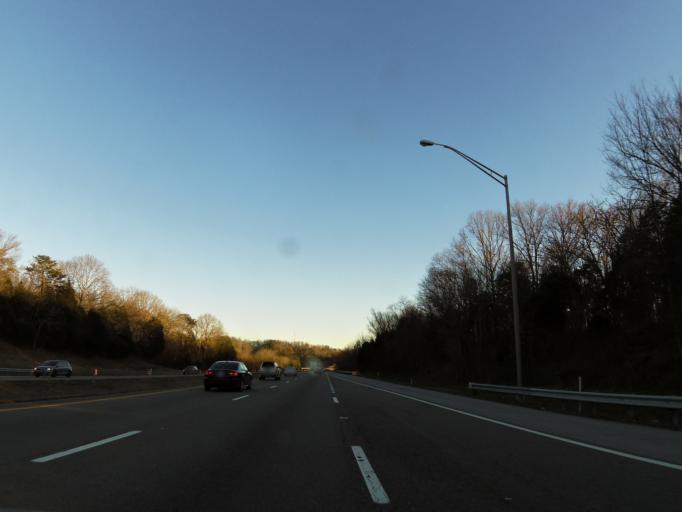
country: US
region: Tennessee
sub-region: Anderson County
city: Norris
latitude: 36.1628
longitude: -84.0777
